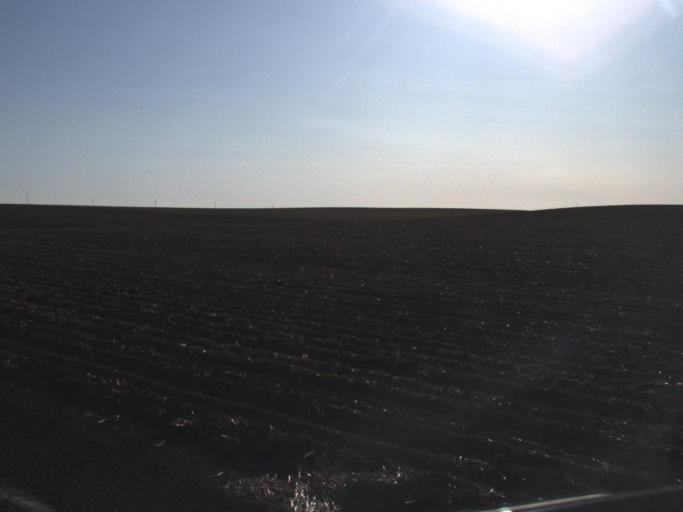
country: US
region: Washington
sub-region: Adams County
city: Ritzville
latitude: 47.0835
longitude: -118.3654
